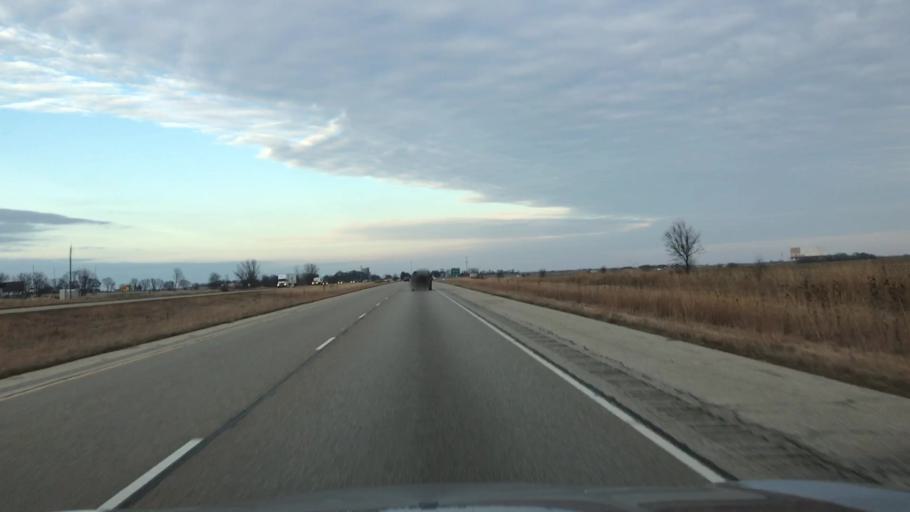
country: US
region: Illinois
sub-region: McLean County
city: Twin Grove
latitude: 40.3902
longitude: -89.0801
